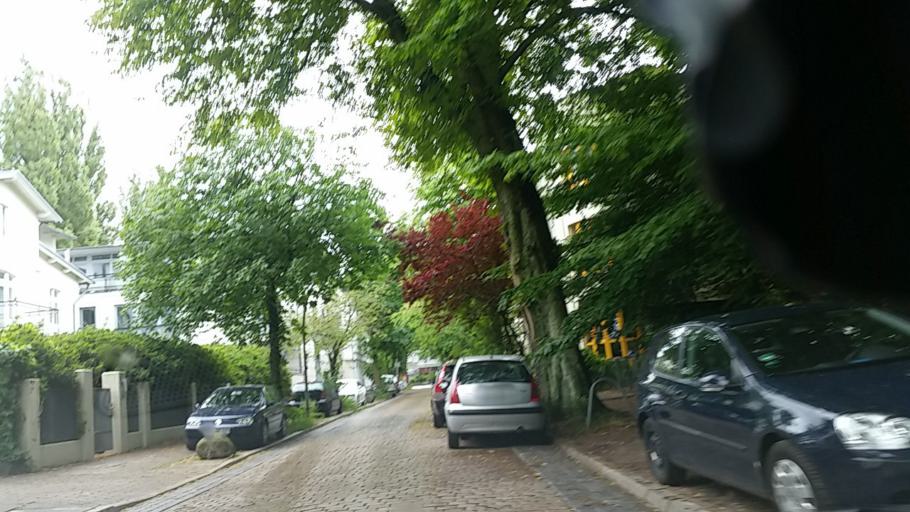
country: DE
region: Hamburg
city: Altona
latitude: 53.5472
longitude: 9.9221
